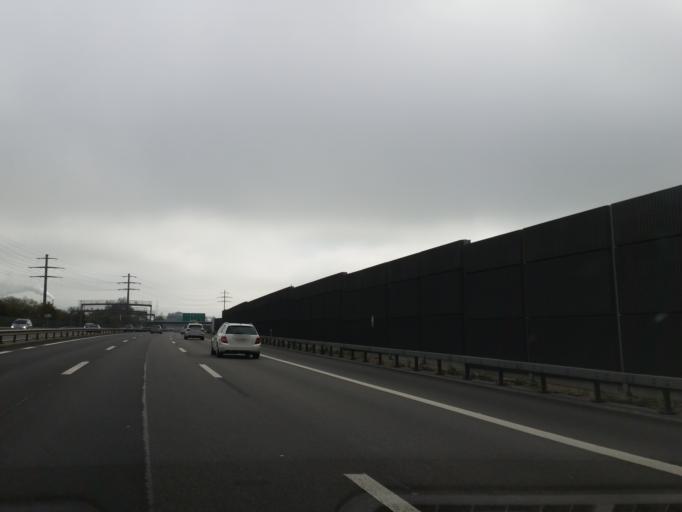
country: CH
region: Aargau
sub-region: Bezirk Zofingen
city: Aarburg
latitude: 47.3099
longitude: 7.9027
